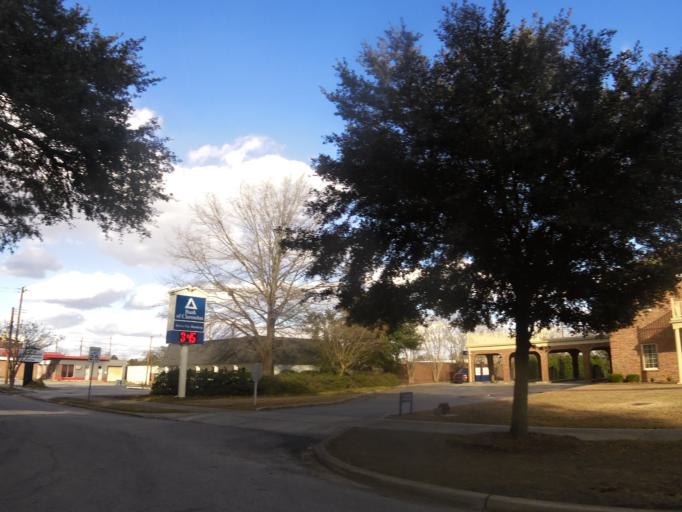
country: US
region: South Carolina
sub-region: Clarendon County
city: Manning
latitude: 33.6934
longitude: -80.2107
